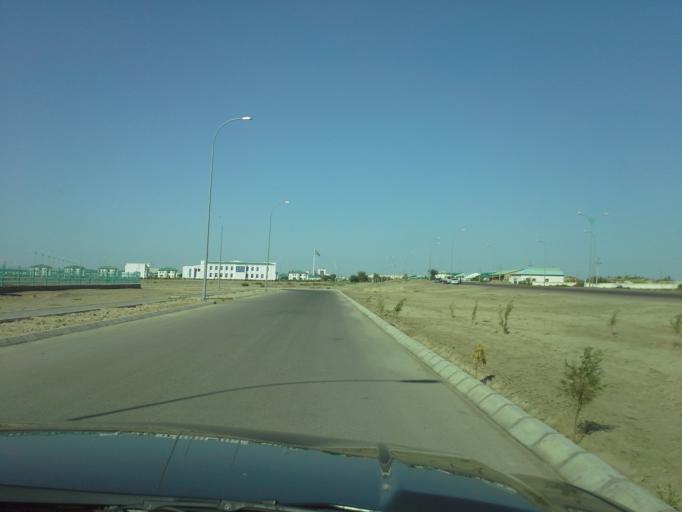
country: TM
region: Dasoguz
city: Dasoguz
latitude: 41.8095
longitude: 59.9571
